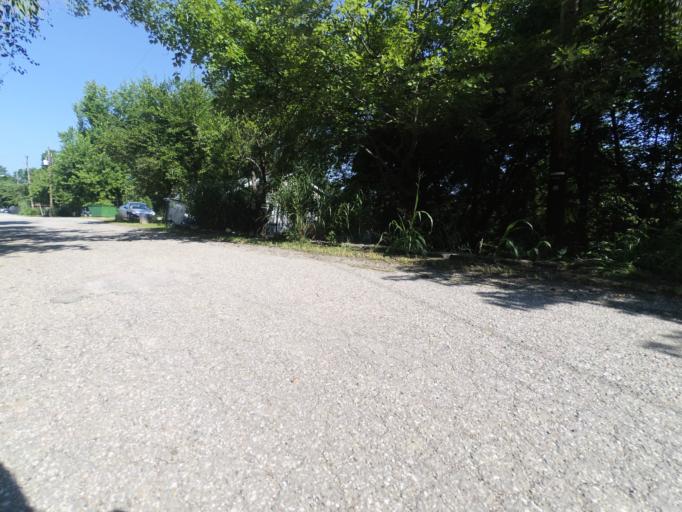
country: US
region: West Virginia
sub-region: Cabell County
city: Huntington
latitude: 38.4365
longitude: -82.4375
